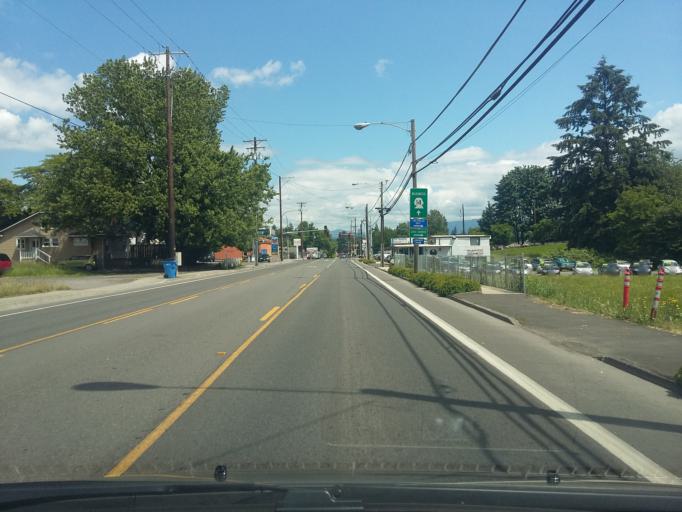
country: US
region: Washington
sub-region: Clark County
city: Washougal
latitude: 45.5812
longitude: -122.3557
